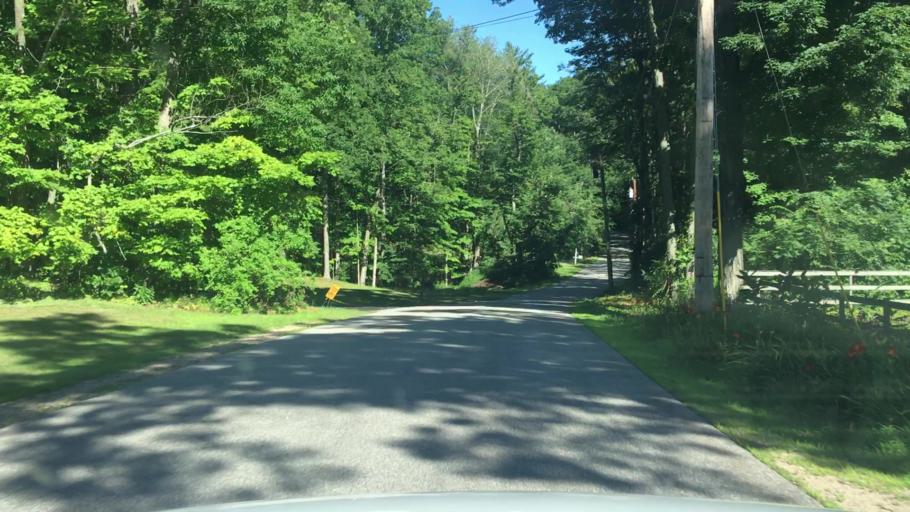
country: US
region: New Hampshire
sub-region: Rockingham County
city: Kensington
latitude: 42.9153
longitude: -70.9333
